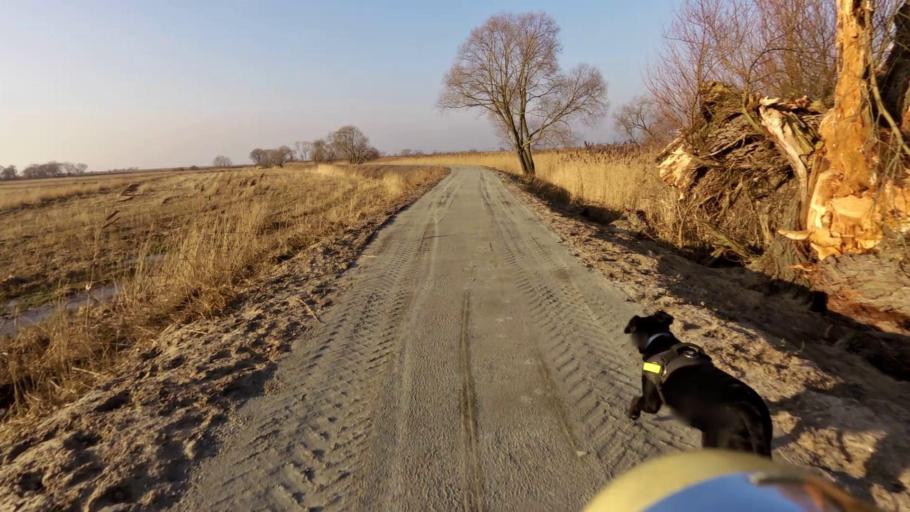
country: PL
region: West Pomeranian Voivodeship
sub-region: Powiat kamienski
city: Wolin
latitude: 53.7555
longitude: 14.5737
